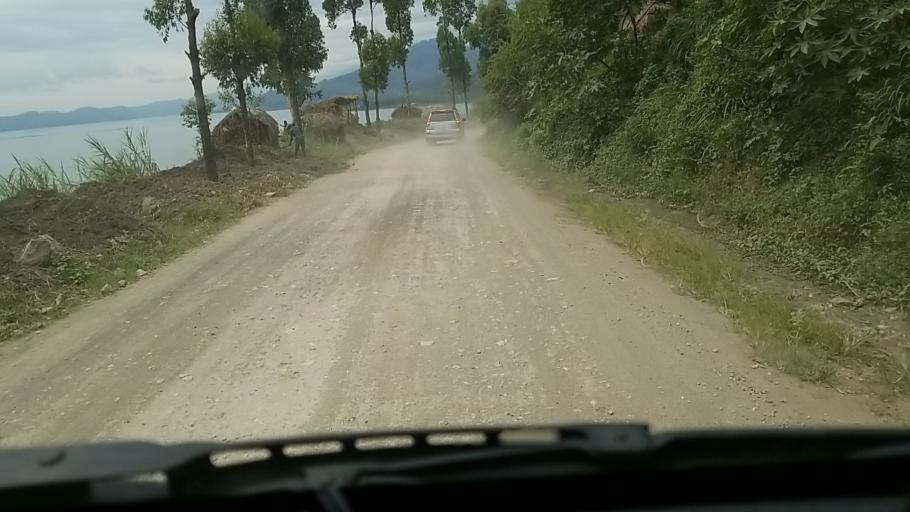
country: CD
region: Nord Kivu
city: Sake
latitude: -1.5893
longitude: 29.0460
